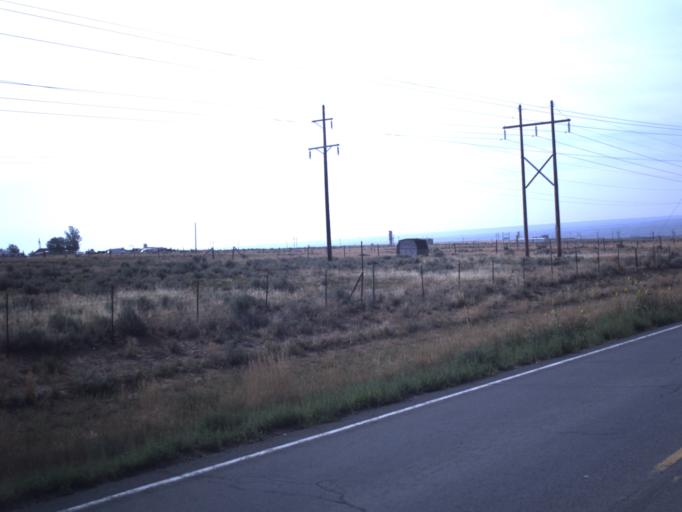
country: US
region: Utah
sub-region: Duchesne County
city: Duchesne
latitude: 40.2217
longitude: -110.3893
